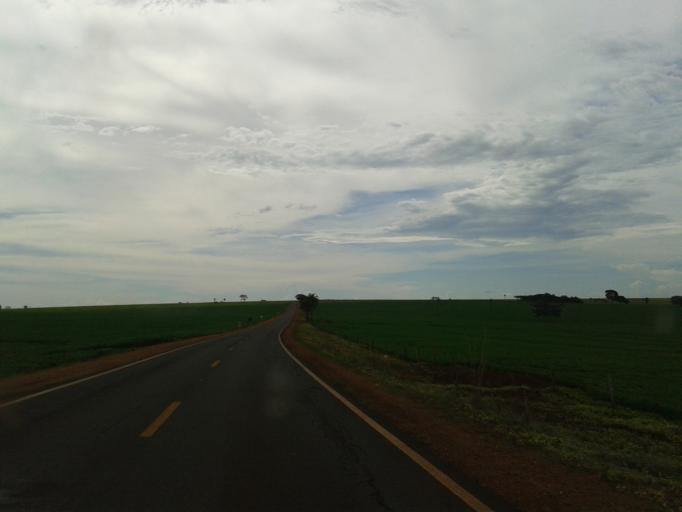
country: BR
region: Minas Gerais
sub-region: Capinopolis
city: Capinopolis
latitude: -18.6931
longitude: -49.4874
